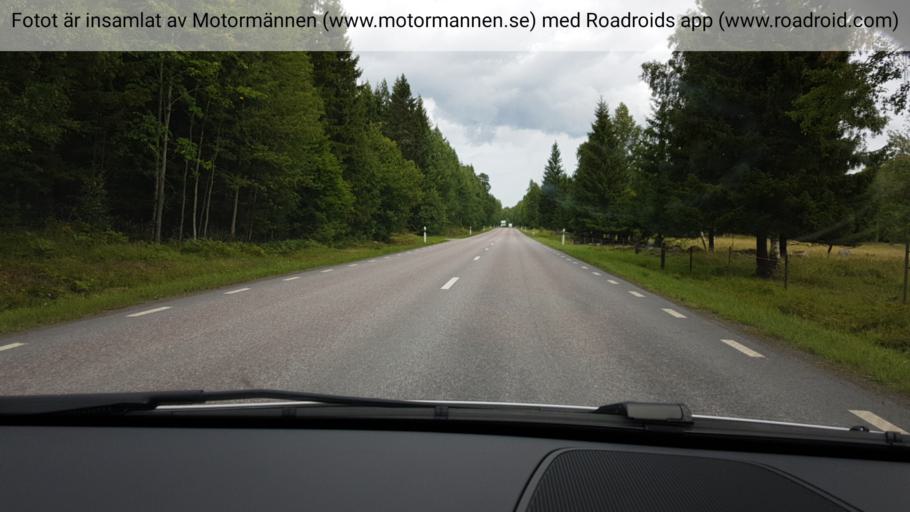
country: SE
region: Uppsala
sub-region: Osthammars Kommun
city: Gimo
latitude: 60.1951
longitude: 18.1929
